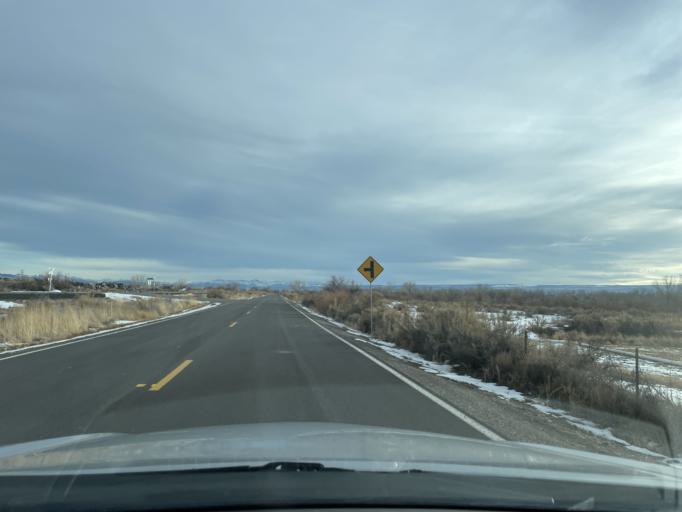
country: US
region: Colorado
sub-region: Montrose County
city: Olathe
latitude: 38.6503
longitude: -107.9957
